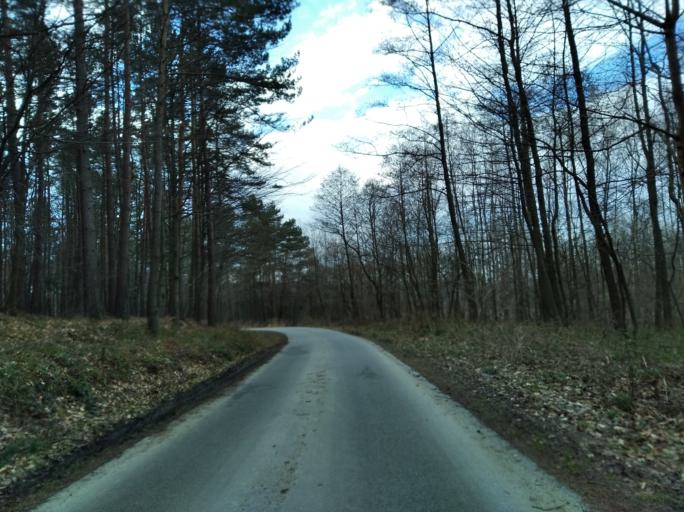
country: PL
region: Subcarpathian Voivodeship
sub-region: Powiat strzyzowski
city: Wysoka Strzyzowska
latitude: 49.7982
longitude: 21.7294
